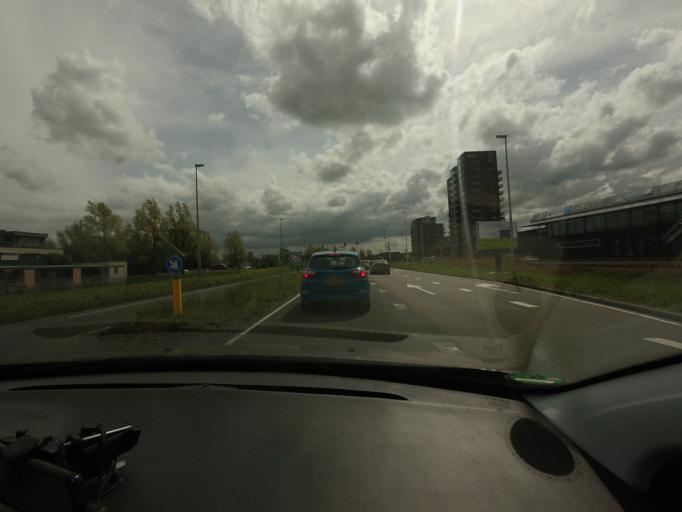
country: NL
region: North Holland
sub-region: Gemeente Purmerend
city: Purmerend
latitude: 52.4966
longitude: 4.9400
